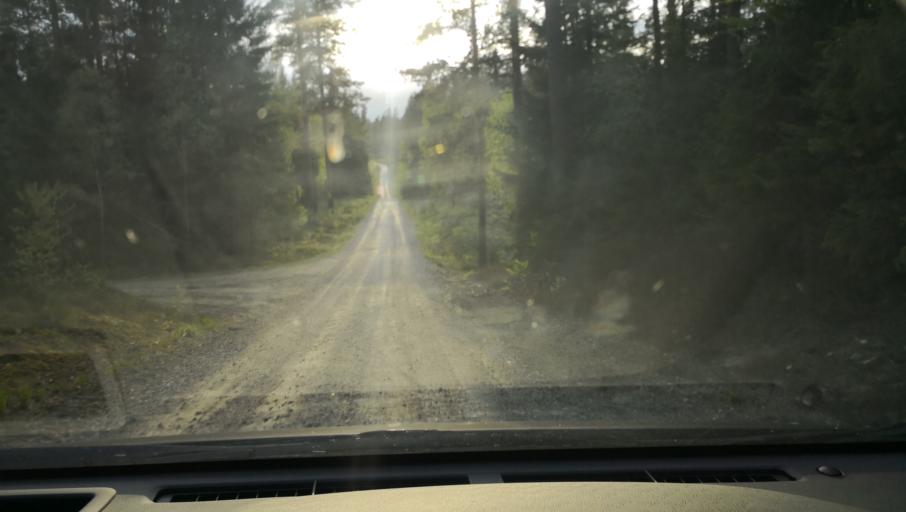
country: SE
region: Vaestmanland
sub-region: Skinnskattebergs Kommun
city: Skinnskatteberg
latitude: 59.7993
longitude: 15.4844
